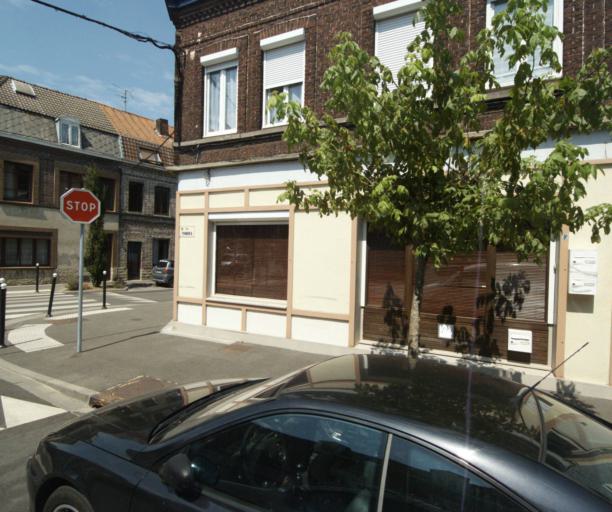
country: FR
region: Nord-Pas-de-Calais
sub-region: Departement du Nord
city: Saint-Andre-lez-Lille
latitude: 50.6567
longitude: 3.0533
